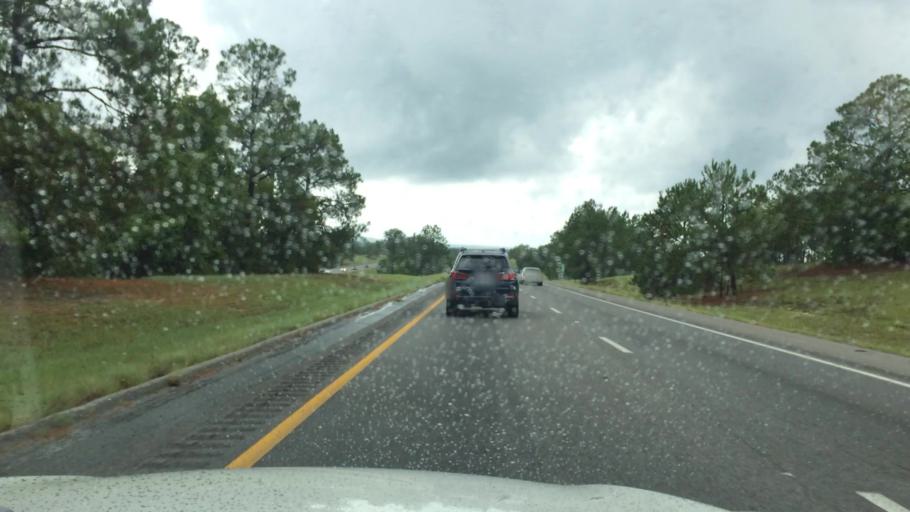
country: US
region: South Carolina
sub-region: Kershaw County
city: Lugoff
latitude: 34.1632
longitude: -80.7218
